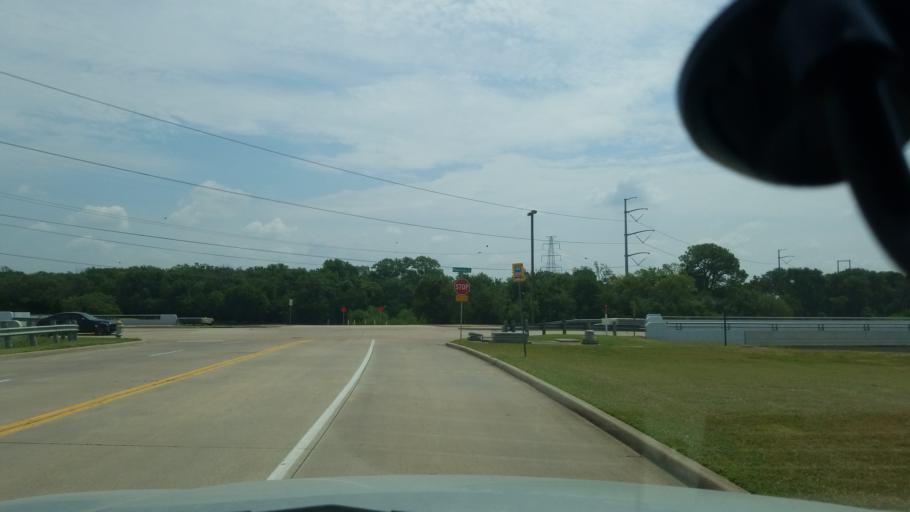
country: US
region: Texas
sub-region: Dallas County
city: Farmers Branch
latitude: 32.8856
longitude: -96.9345
